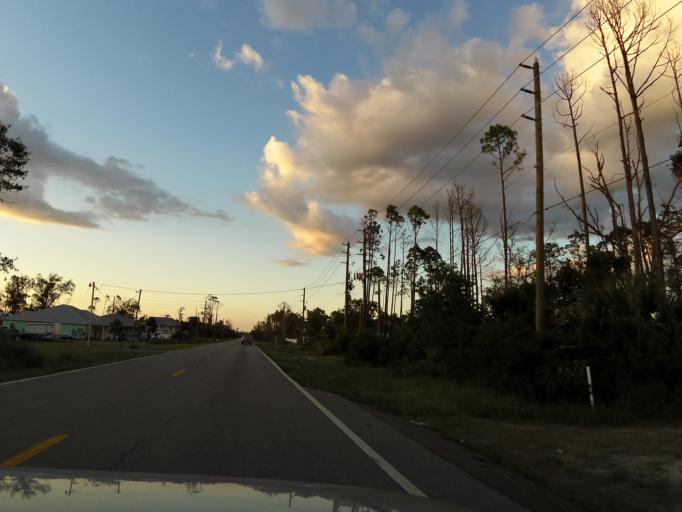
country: US
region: Florida
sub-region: Bay County
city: Mexico Beach
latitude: 29.9283
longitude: -85.3884
